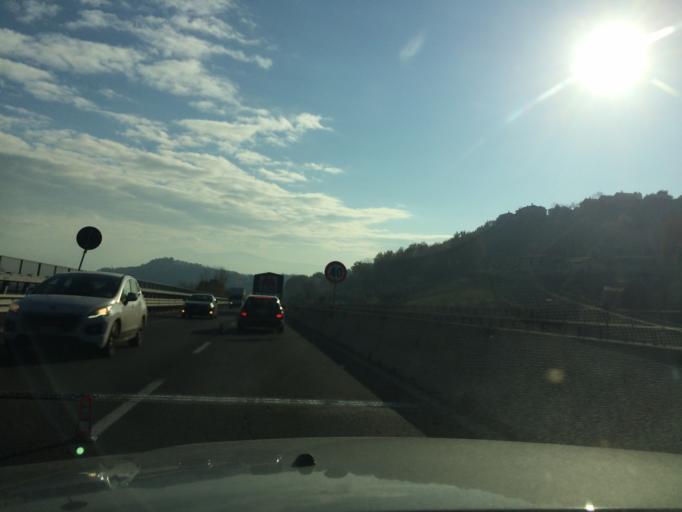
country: IT
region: Umbria
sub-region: Provincia di Terni
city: San Gemini
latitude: 42.6149
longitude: 12.5543
